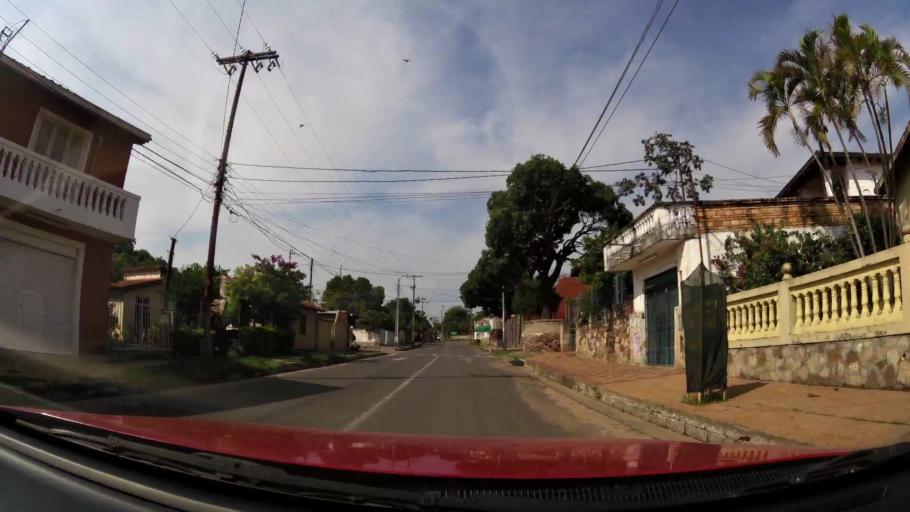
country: PY
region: Central
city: Fernando de la Mora
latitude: -25.2671
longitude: -57.5491
